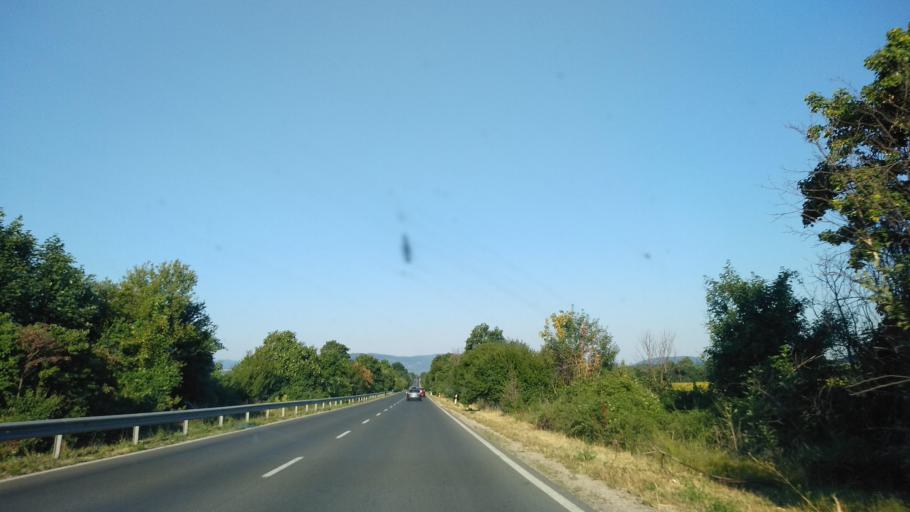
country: BG
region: Gabrovo
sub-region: Obshtina Sevlievo
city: Sevlievo
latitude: 43.0364
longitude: 25.1459
